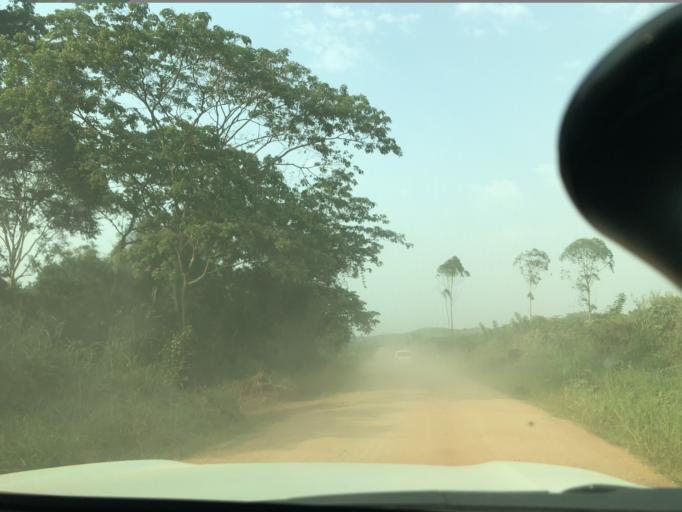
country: UG
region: Western Region
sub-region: Kasese District
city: Margherita
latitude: 0.1782
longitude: 29.6586
